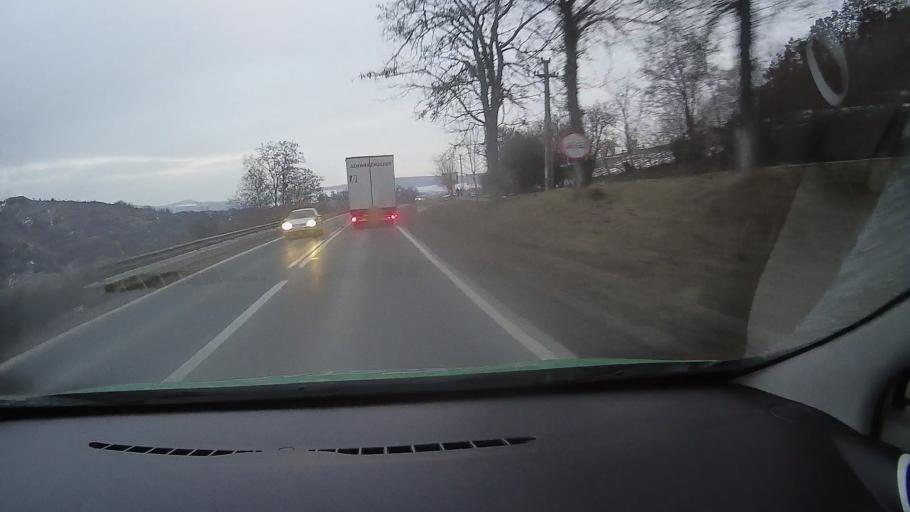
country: RO
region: Harghita
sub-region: Municipiul Odorheiu Secuiesc
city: Odorheiu Secuiesc
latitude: 46.3254
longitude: 25.2793
